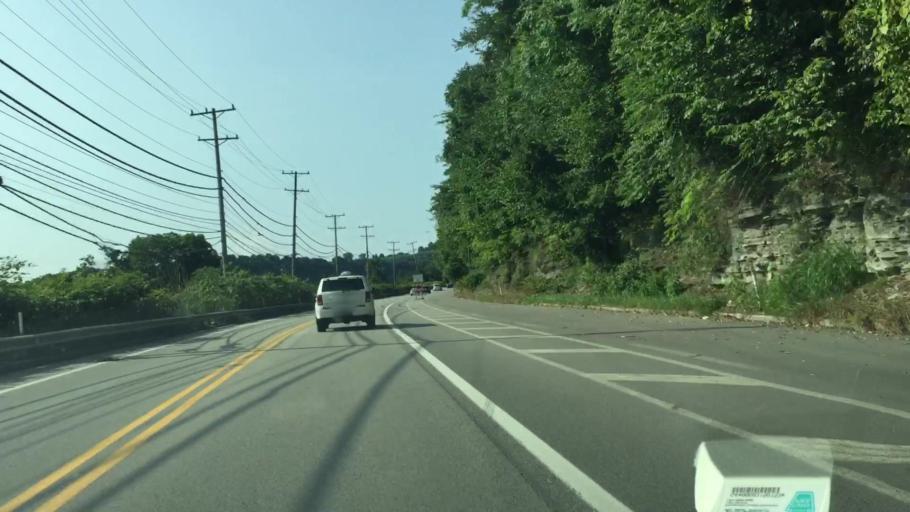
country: US
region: Pennsylvania
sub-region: Allegheny County
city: Verona
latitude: 40.5042
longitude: -79.8513
